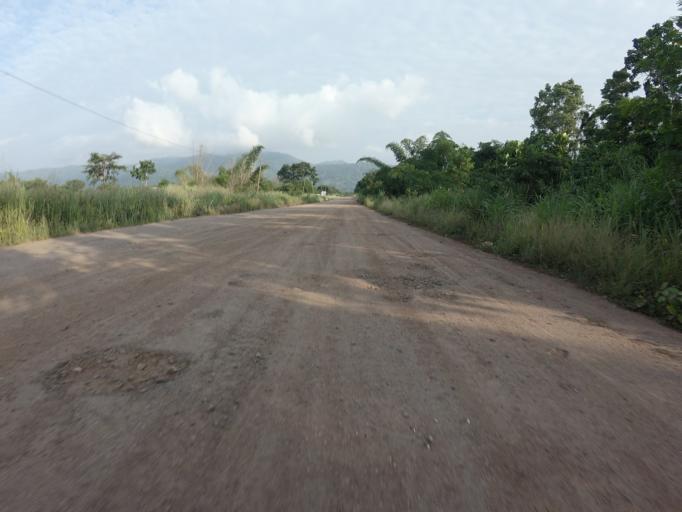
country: GH
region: Volta
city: Kpandu
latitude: 6.9475
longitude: 0.4600
